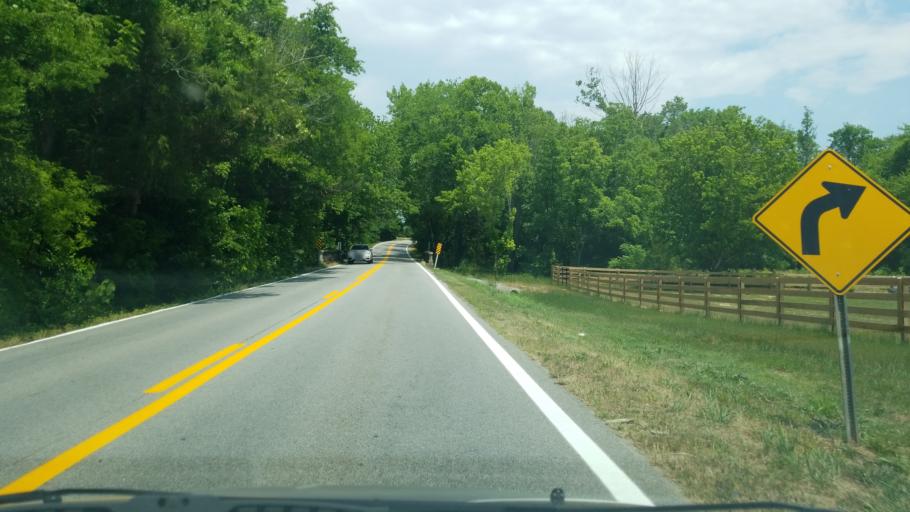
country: US
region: Tennessee
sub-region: Hamilton County
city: East Brainerd
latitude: 34.9906
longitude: -85.0965
